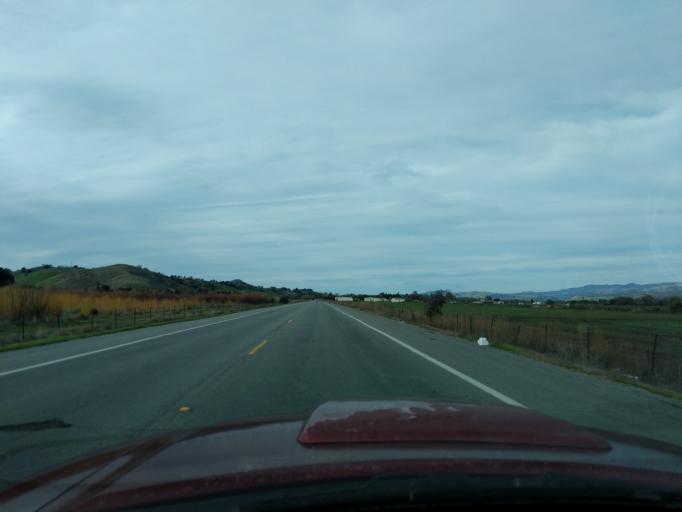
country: US
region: California
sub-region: Santa Clara County
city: San Martin
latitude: 37.0609
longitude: -121.6097
